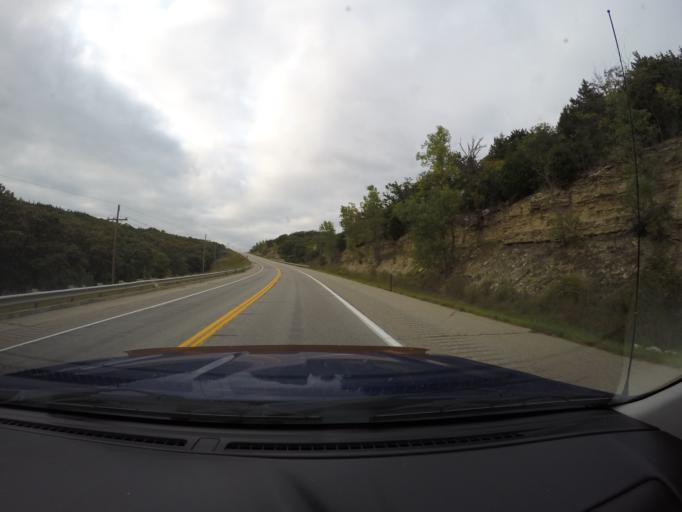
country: US
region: Kansas
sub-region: Riley County
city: Manhattan
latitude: 39.1707
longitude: -96.6443
